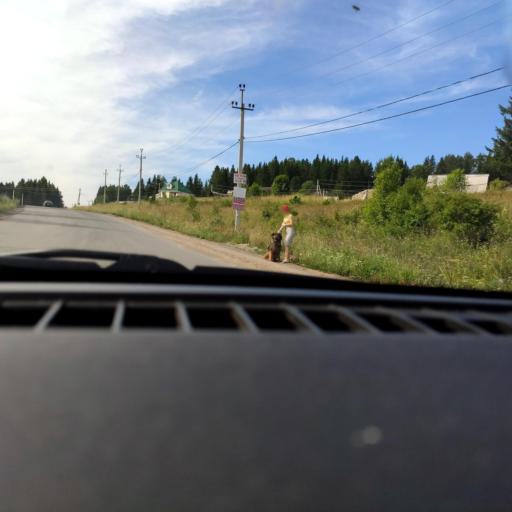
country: RU
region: Perm
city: Polazna
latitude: 58.3489
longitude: 56.2509
